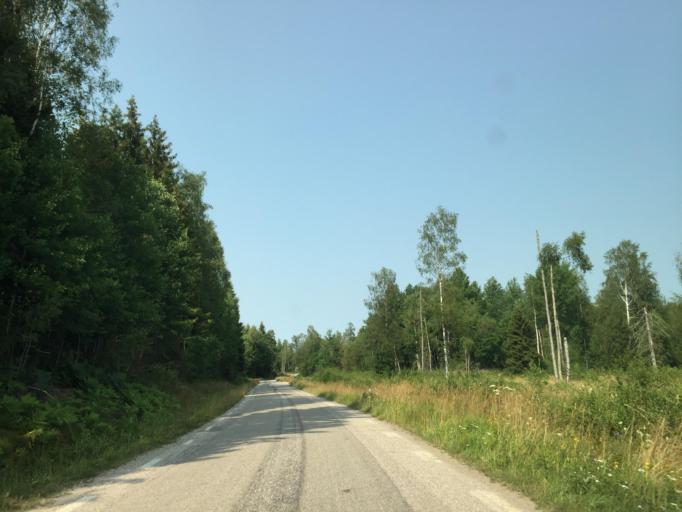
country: SE
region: Vaestra Goetaland
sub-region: Trollhattan
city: Sjuntorp
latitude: 58.2947
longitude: 12.1441
